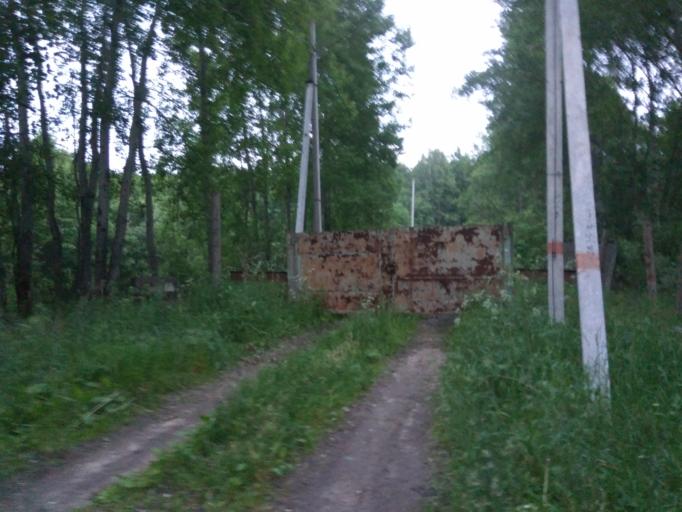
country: RU
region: Moskovskaya
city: Malyshevo
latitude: 55.5609
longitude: 38.3279
